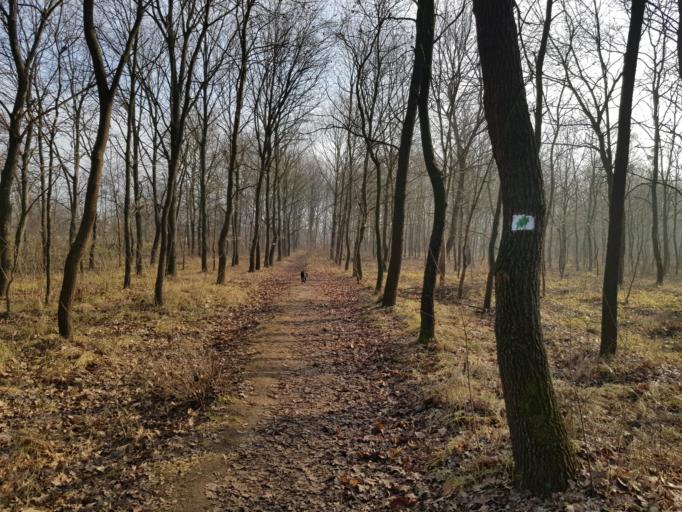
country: HU
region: Budapest
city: Budapest XVII. keruelet
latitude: 47.4714
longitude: 19.2167
